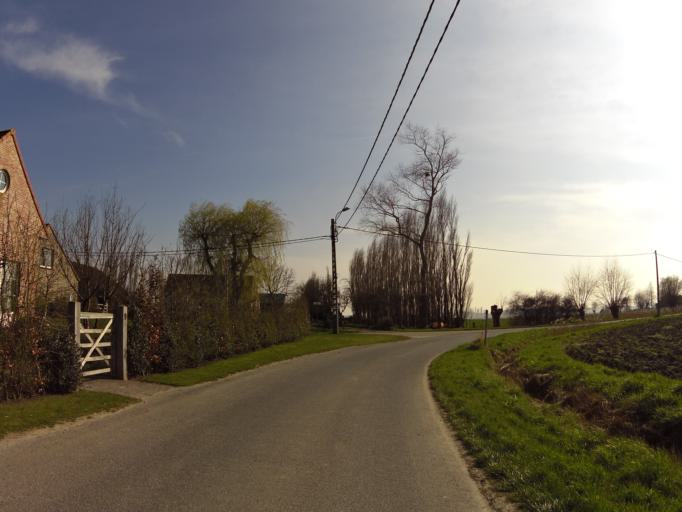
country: BE
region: Flanders
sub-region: Provincie West-Vlaanderen
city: Oudenburg
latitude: 51.1940
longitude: 3.0417
